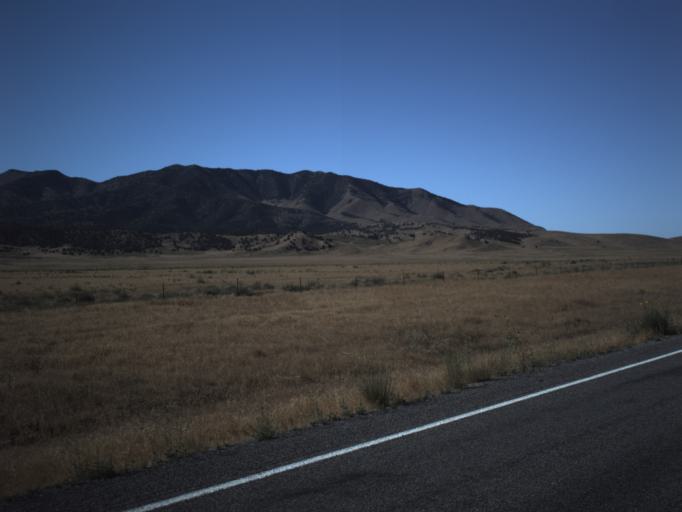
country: US
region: Utah
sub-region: Juab County
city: Nephi
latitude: 39.6842
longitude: -112.2461
